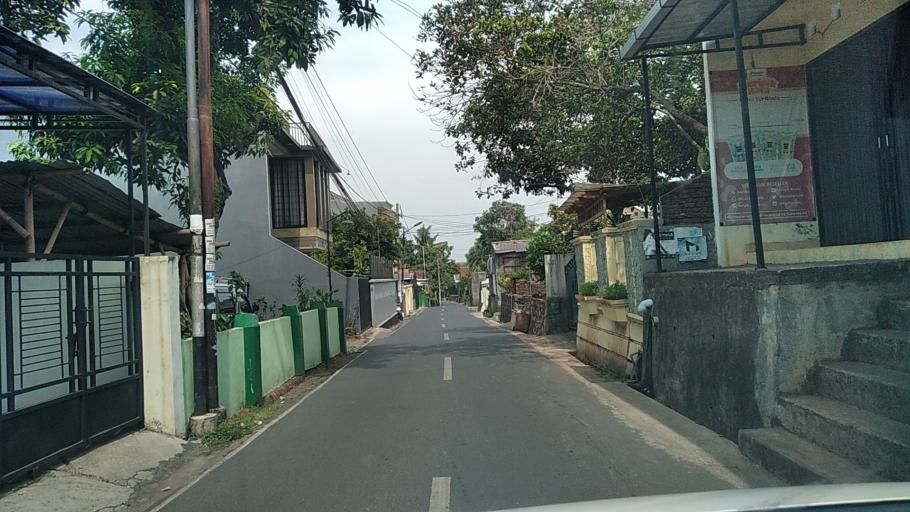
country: ID
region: Central Java
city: Semarang
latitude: -7.0347
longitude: 110.4278
